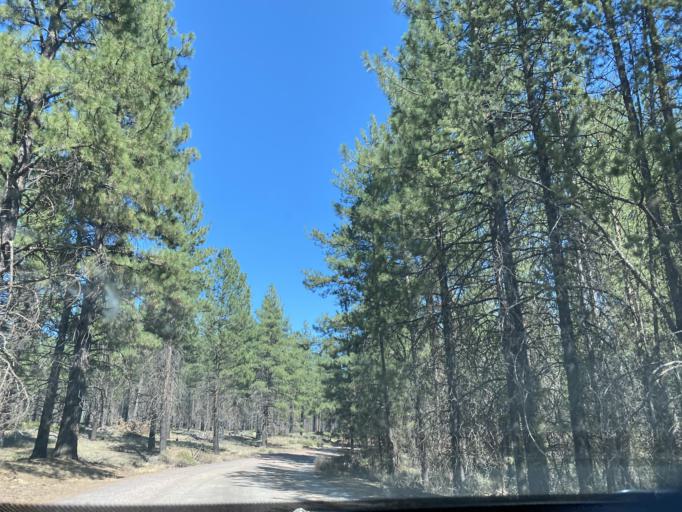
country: US
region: Oregon
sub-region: Deschutes County
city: Sunriver
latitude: 43.8710
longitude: -121.4793
